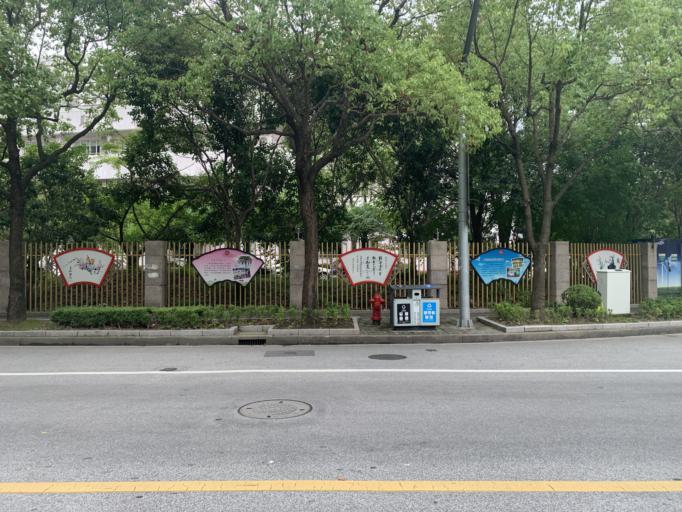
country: CN
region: Shanghai Shi
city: Huamu
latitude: 31.2286
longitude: 121.5574
